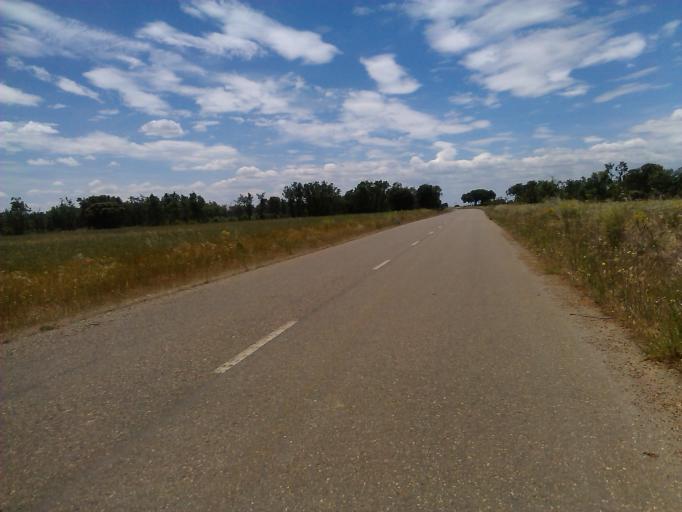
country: ES
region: Castille and Leon
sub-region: Provincia de Leon
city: Chozas de Abajo
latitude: 42.4973
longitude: -5.7060
